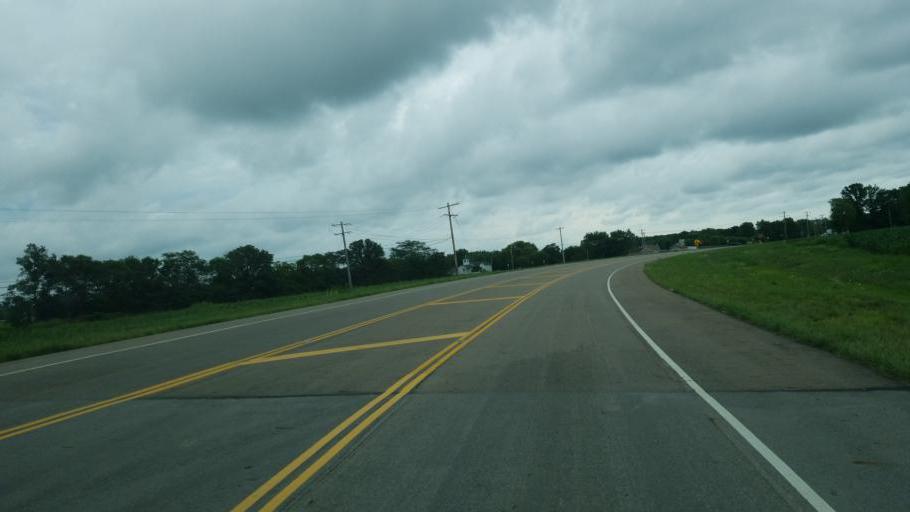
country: US
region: Ohio
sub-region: Pickaway County
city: Ashville
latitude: 39.7713
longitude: -82.9529
